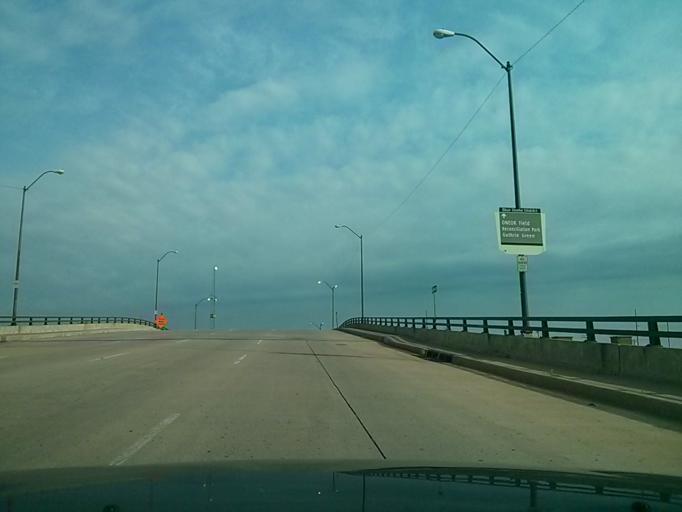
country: US
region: Oklahoma
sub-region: Tulsa County
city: Tulsa
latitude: 36.1568
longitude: -95.9886
